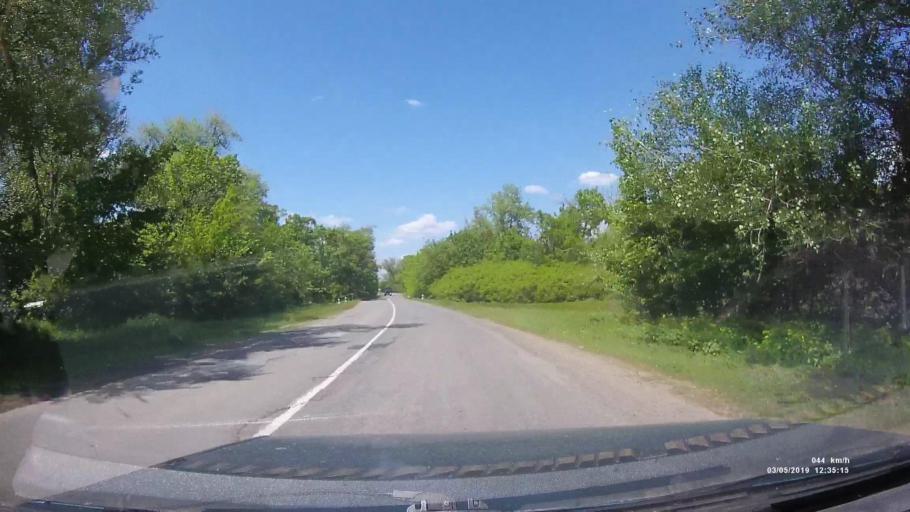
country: RU
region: Rostov
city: Semikarakorsk
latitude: 47.5252
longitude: 40.7621
